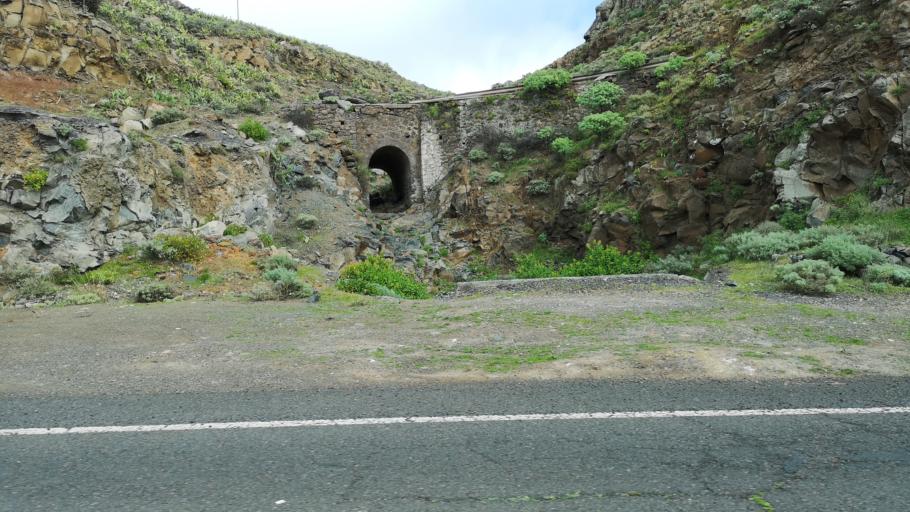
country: ES
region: Canary Islands
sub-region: Provincia de Santa Cruz de Tenerife
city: Vallehermosa
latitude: 28.1259
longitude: -17.3213
